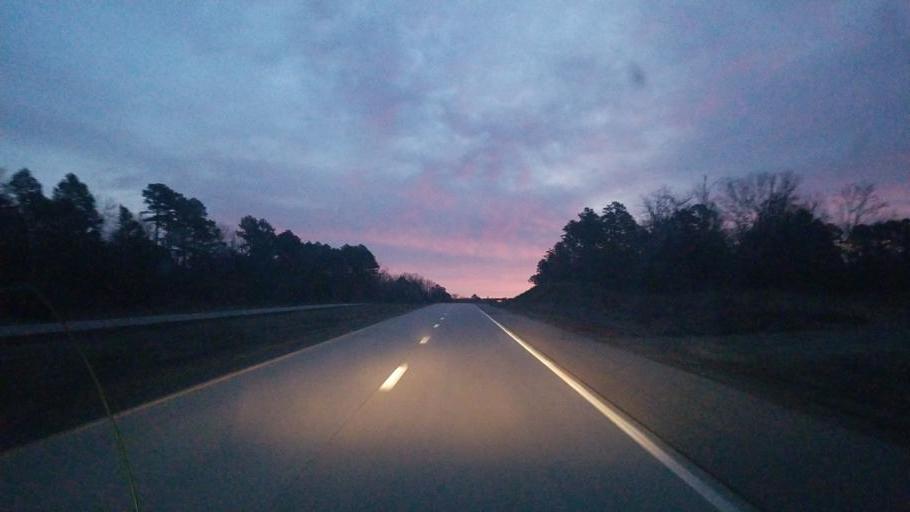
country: US
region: Missouri
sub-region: Shannon County
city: Winona
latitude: 36.9988
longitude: -91.4286
